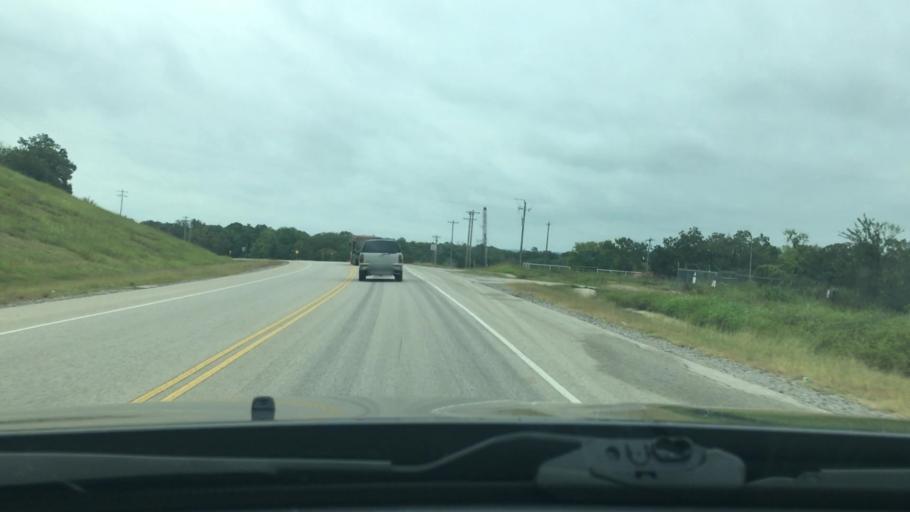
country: US
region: Oklahoma
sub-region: Pontotoc County
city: Ada
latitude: 34.6060
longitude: -96.6338
